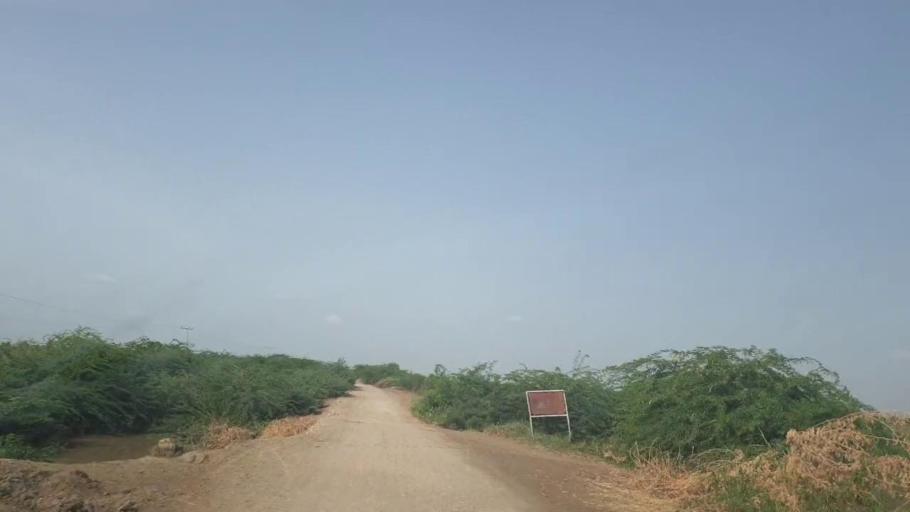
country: PK
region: Sindh
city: Tando Bago
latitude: 24.7870
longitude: 69.1329
